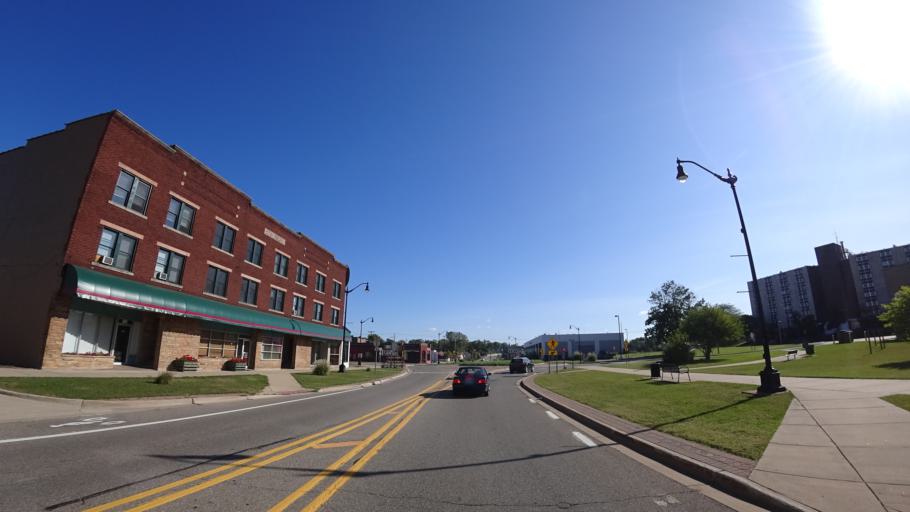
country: US
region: Michigan
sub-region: Berrien County
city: Benton Harbor
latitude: 42.1164
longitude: -86.4536
